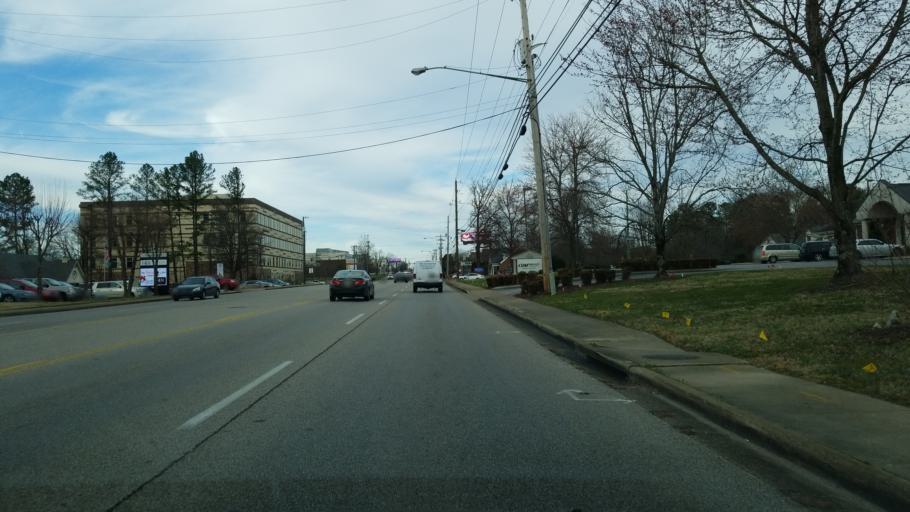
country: US
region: Tennessee
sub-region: Hamilton County
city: East Brainerd
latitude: 35.0192
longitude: -85.1614
